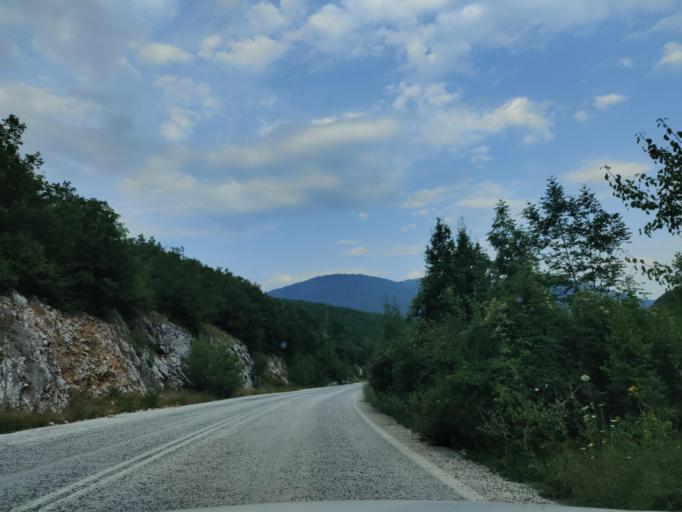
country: GR
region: East Macedonia and Thrace
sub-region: Nomos Dramas
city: Volakas
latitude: 41.2918
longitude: 23.9595
